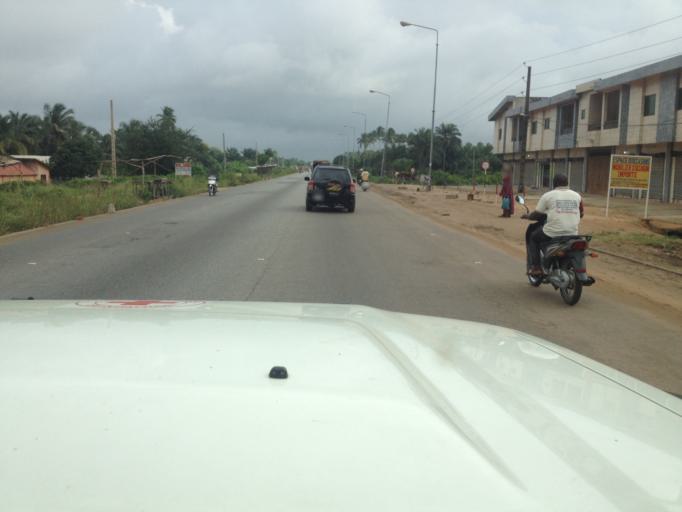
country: BJ
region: Queme
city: Porto-Novo
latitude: 6.4360
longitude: 2.6243
